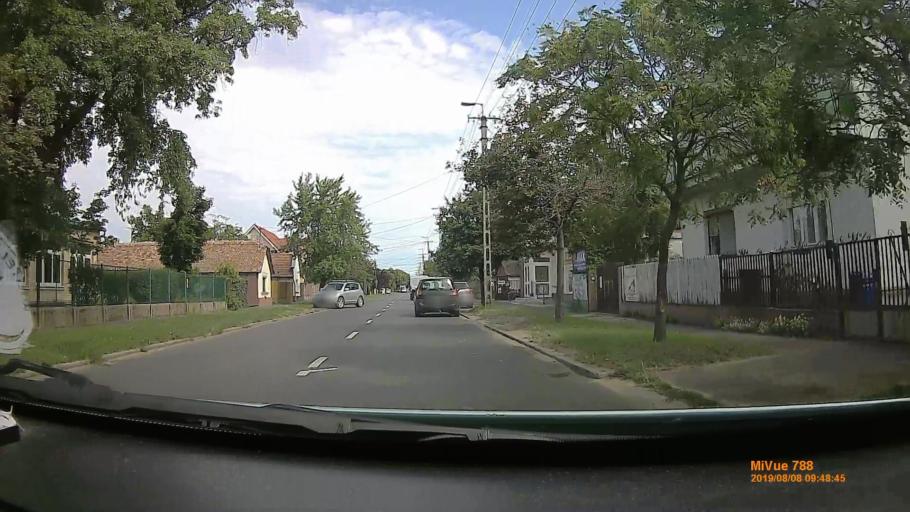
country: HU
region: Hajdu-Bihar
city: Debrecen
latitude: 47.5427
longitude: 21.6539
